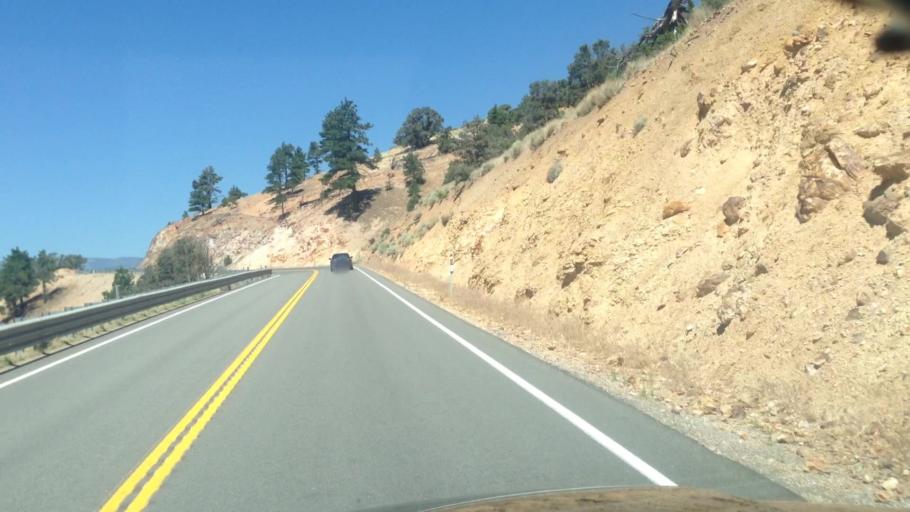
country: US
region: Nevada
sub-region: Storey County
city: Virginia City
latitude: 39.3895
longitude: -119.7066
